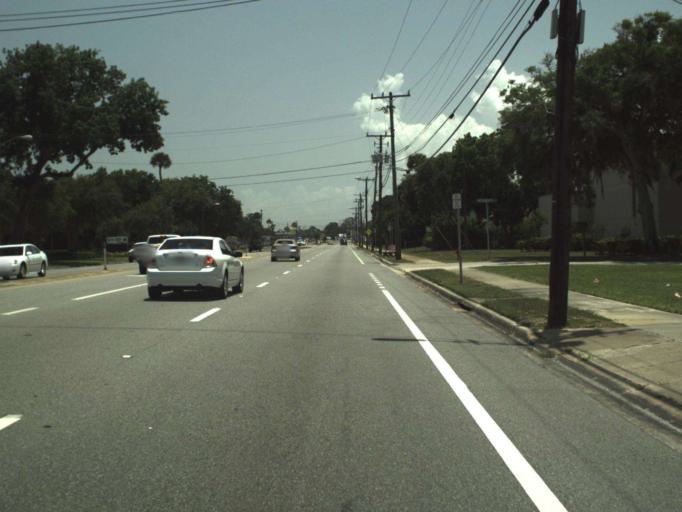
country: US
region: Florida
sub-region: Volusia County
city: Edgewater
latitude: 28.9969
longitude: -80.9106
